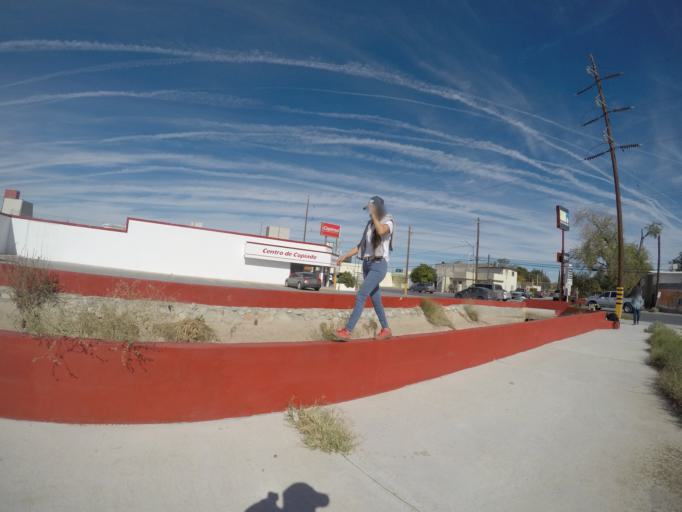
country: MX
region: Chihuahua
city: Ciudad Juarez
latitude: 31.7351
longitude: -106.4408
